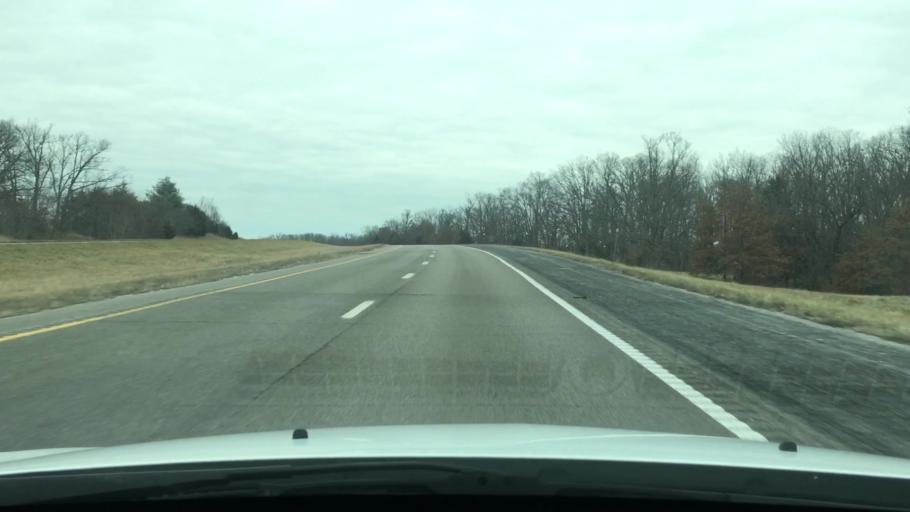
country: US
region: Missouri
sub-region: Callaway County
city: Fulton
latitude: 38.9746
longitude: -91.8957
